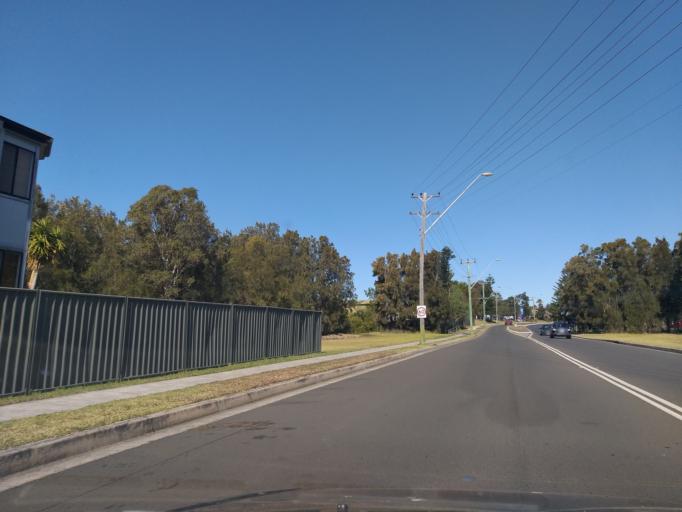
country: AU
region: New South Wales
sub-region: Wollongong
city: Corrimal
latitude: -34.3875
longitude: 150.9061
